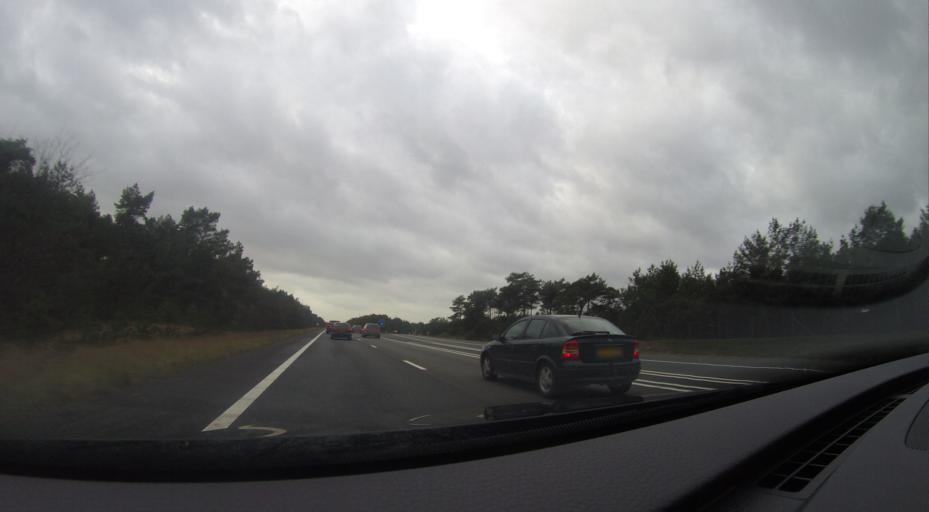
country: NL
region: Gelderland
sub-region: Gemeente Apeldoorn
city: Uddel
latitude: 52.2002
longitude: 5.7843
